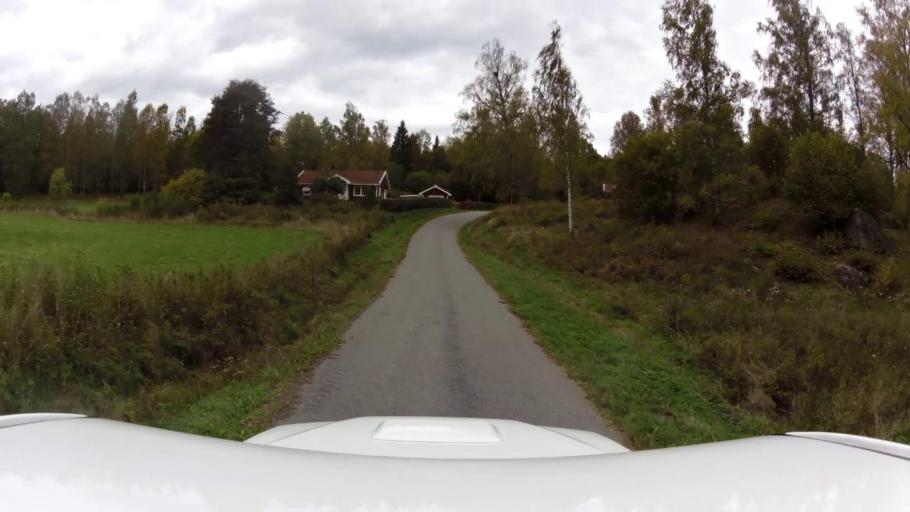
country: SE
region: OEstergoetland
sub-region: Kinda Kommun
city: Rimforsa
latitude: 58.2013
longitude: 15.5567
